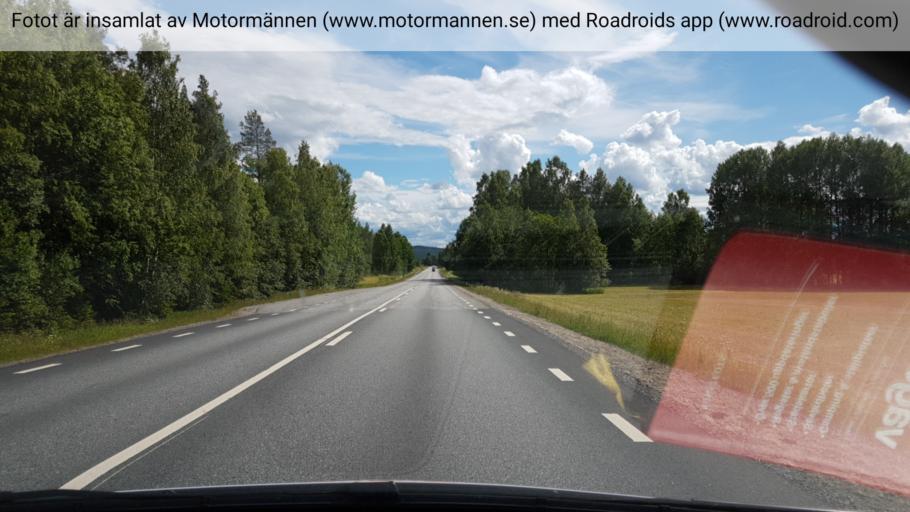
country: SE
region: Vaesternorrland
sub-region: Solleftea Kommun
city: Solleftea
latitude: 63.2678
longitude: 17.2103
